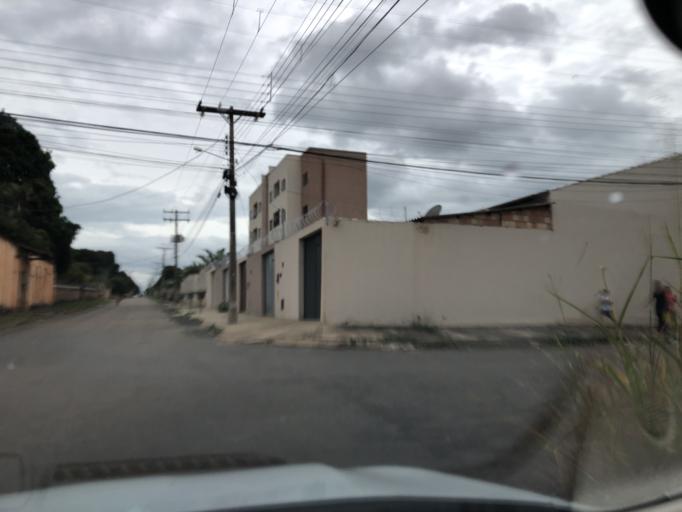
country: BR
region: Goias
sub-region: Luziania
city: Luziania
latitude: -16.1557
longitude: -47.9471
